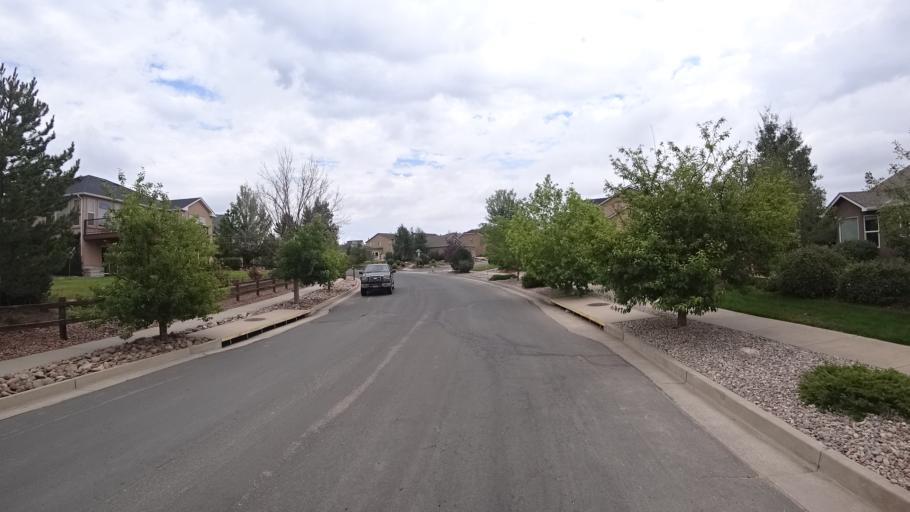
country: US
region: Colorado
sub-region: El Paso County
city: Gleneagle
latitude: 39.0040
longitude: -104.7912
